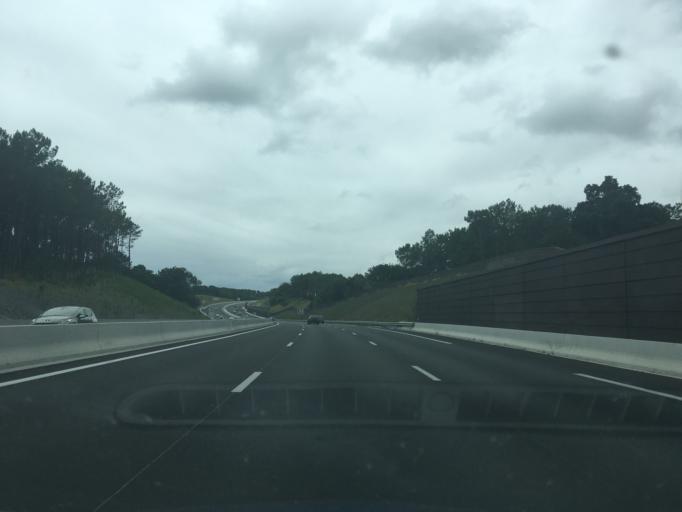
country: FR
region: Aquitaine
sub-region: Departement des Landes
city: Ondres
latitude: 43.5680
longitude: -1.4309
